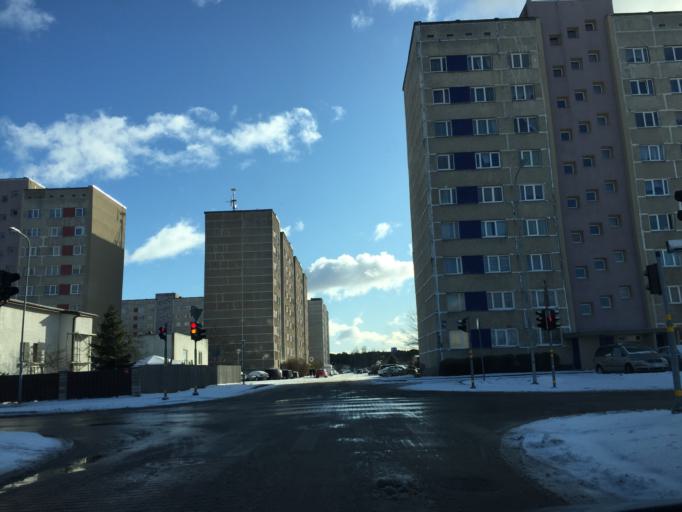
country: LV
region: Ventspils
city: Ventspils
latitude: 57.3844
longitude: 21.5504
